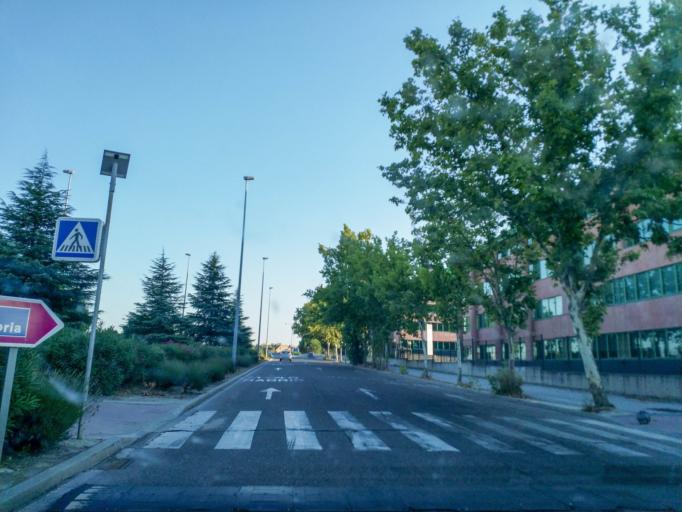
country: ES
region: Madrid
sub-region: Provincia de Madrid
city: Pozuelo de Alarcon
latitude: 40.4628
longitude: -3.8097
